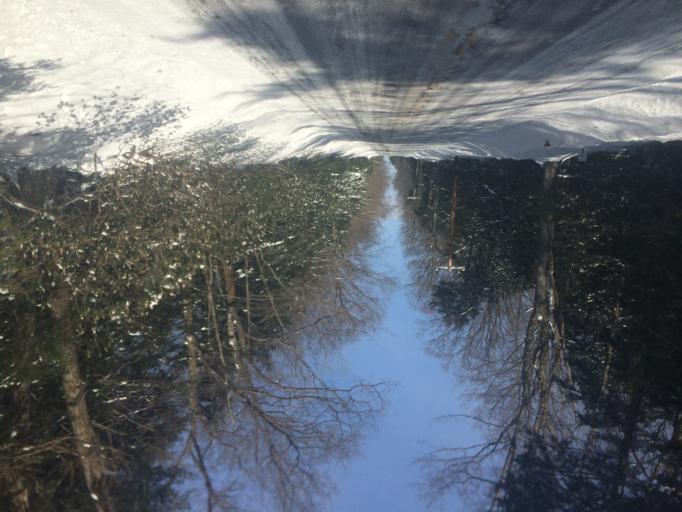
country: US
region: Pennsylvania
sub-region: Centre County
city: Stormstown
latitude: 40.8993
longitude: -78.0473
